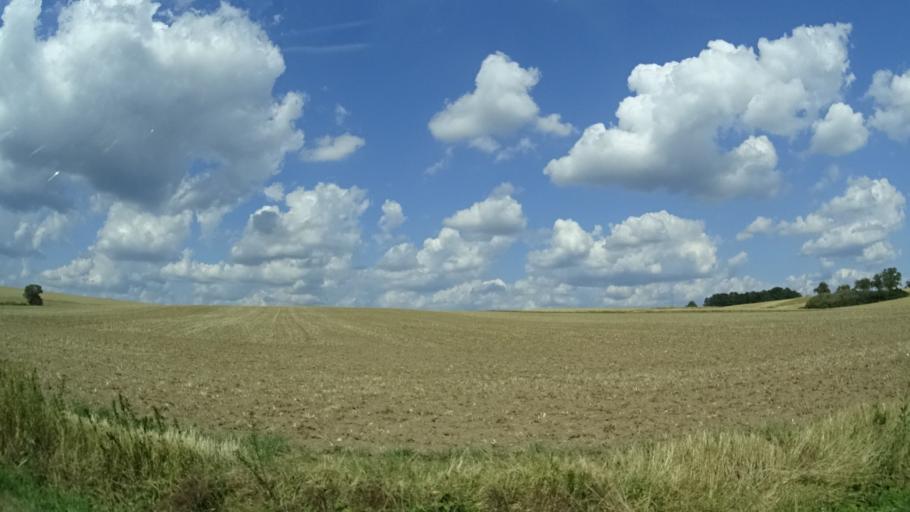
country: DE
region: Thuringia
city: Westhausen
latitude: 50.3609
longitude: 10.6769
